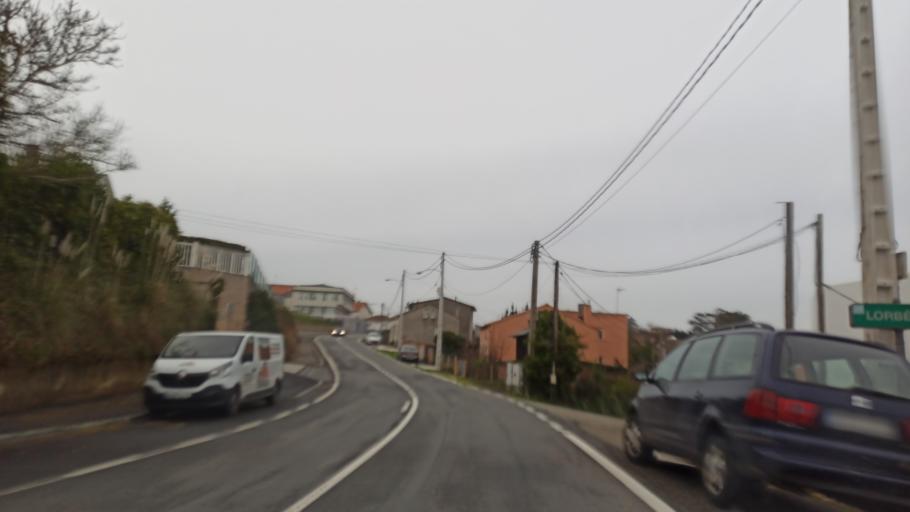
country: ES
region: Galicia
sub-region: Provincia da Coruna
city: Oleiros
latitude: 43.3890
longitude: -8.3055
